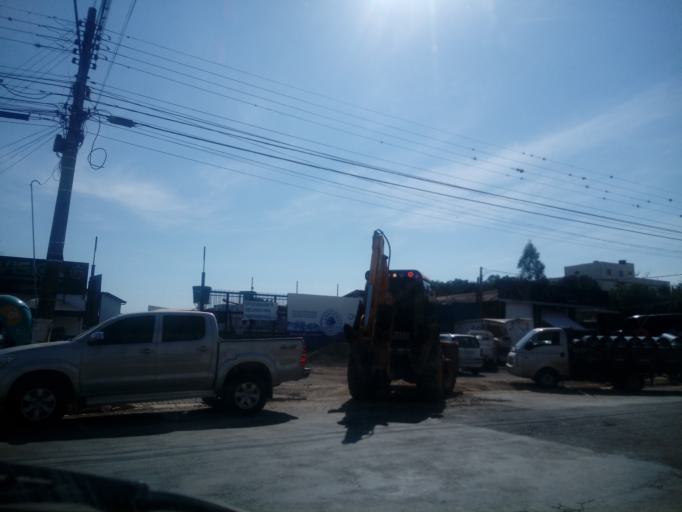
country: BR
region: Santa Catarina
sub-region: Chapeco
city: Chapeco
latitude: -27.0908
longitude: -52.6216
